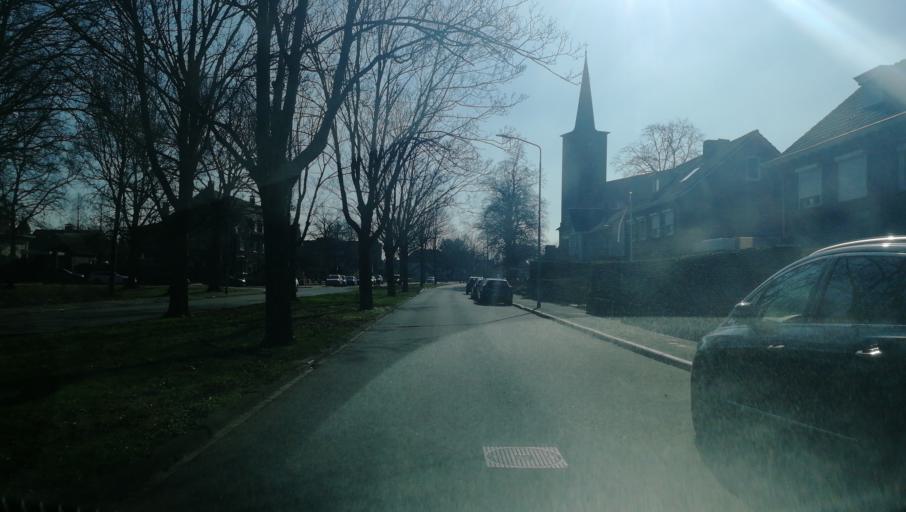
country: NL
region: Limburg
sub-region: Gemeente Venlo
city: Venlo
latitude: 51.3714
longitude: 6.1811
